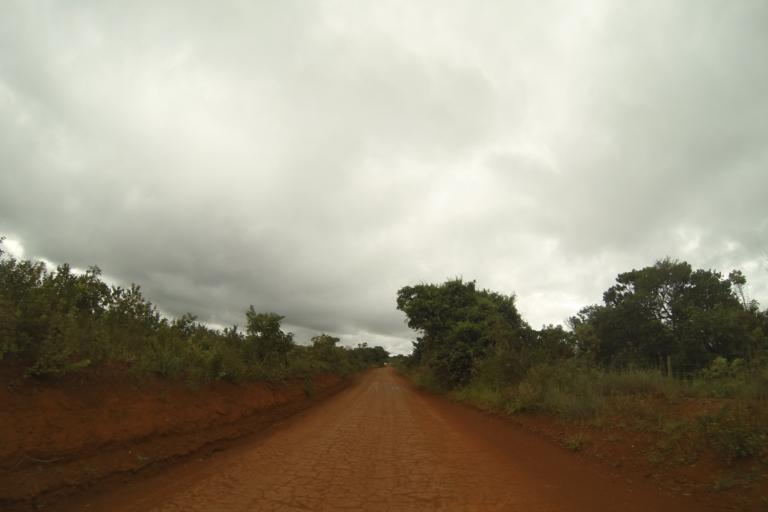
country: BR
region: Minas Gerais
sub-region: Campos Altos
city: Campos Altos
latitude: -19.8266
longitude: -46.3226
